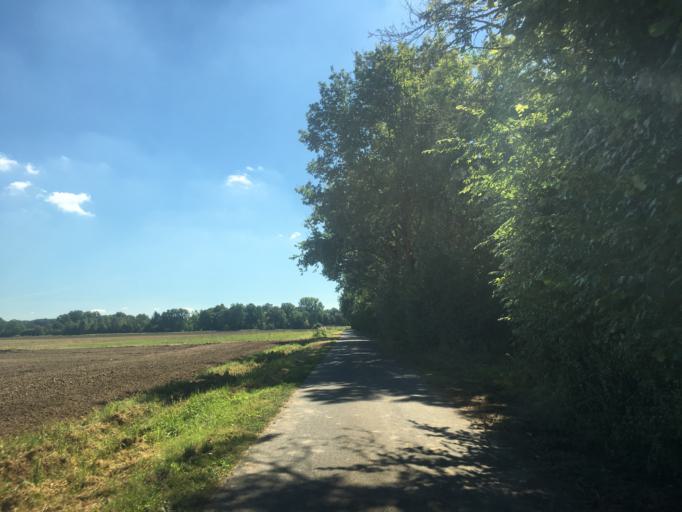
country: DE
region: North Rhine-Westphalia
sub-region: Regierungsbezirk Munster
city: Greven
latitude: 52.0305
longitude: 7.5511
